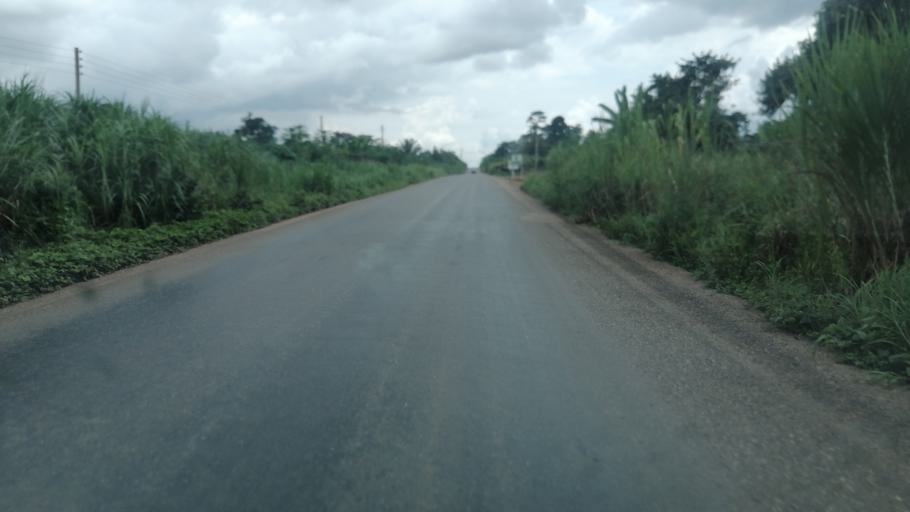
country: GH
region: Western
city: Bibiani
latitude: 6.8708
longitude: -2.4368
